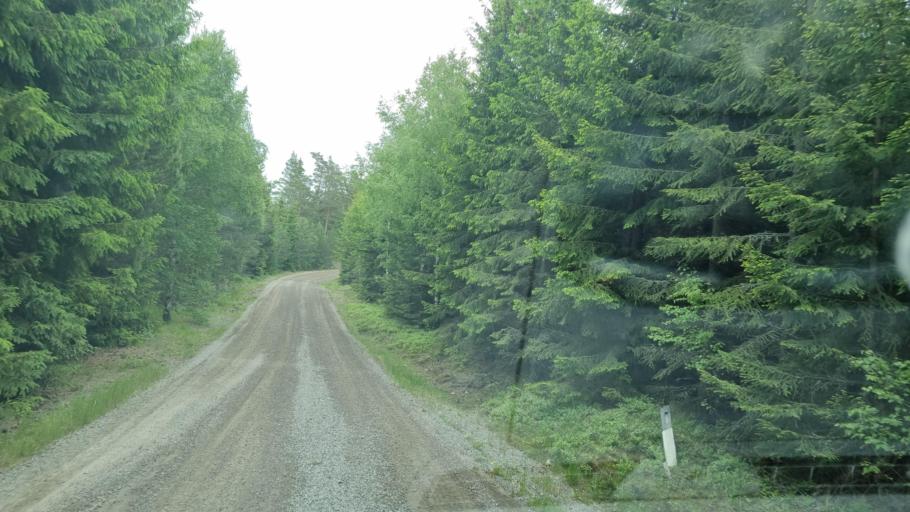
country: SE
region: OEstergoetland
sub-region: Atvidabergs Kommun
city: Atvidaberg
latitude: 58.2592
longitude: 16.0423
